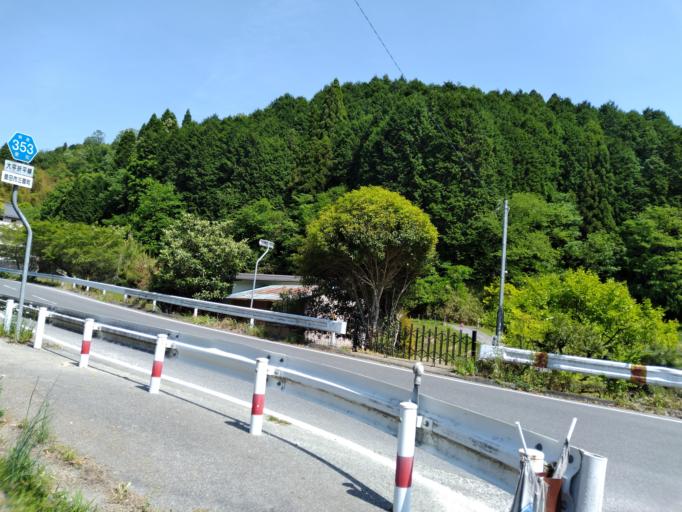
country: JP
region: Gifu
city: Toki
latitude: 35.2430
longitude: 137.2226
